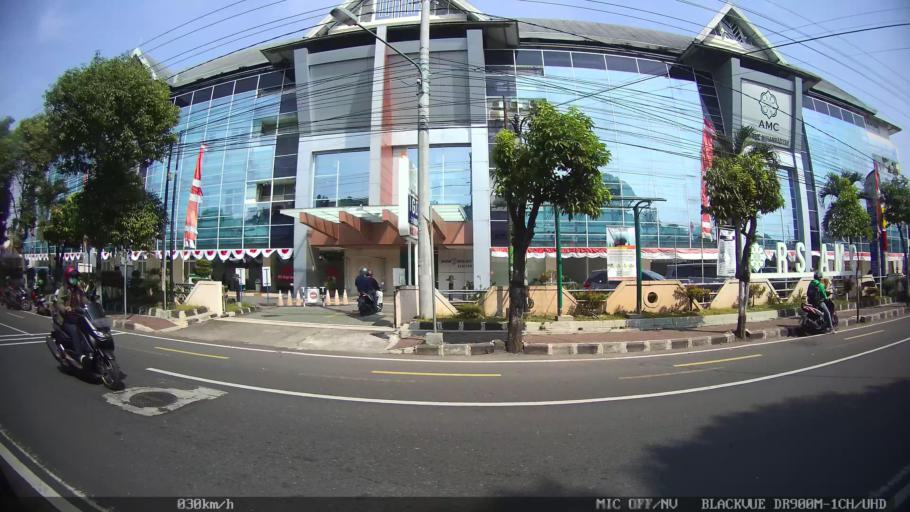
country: ID
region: Daerah Istimewa Yogyakarta
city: Yogyakarta
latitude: -7.7991
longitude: 110.3517
